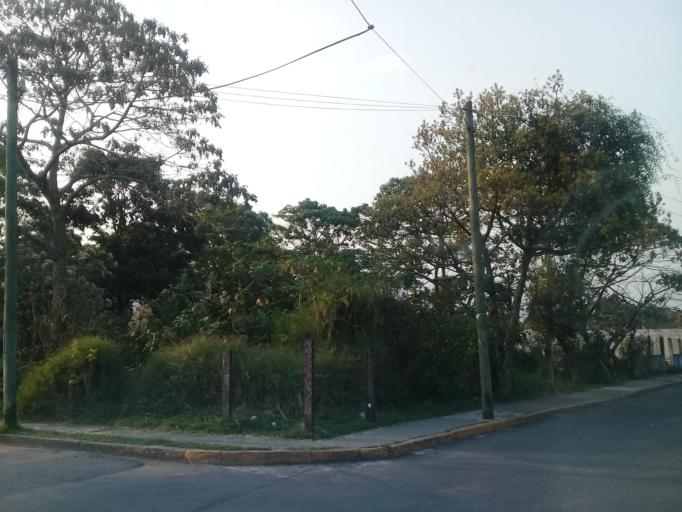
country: MX
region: Veracruz
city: Ixtac Zoquitlan
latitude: 18.8497
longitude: -97.0583
